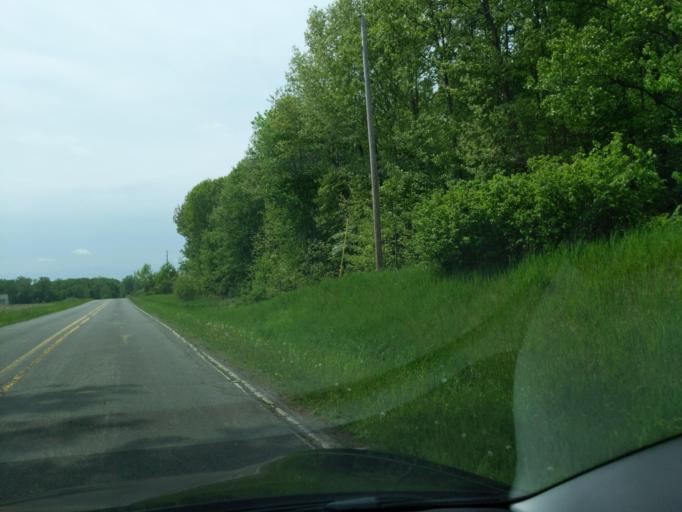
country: US
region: Michigan
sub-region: Ingham County
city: Stockbridge
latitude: 42.4247
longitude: -84.2732
